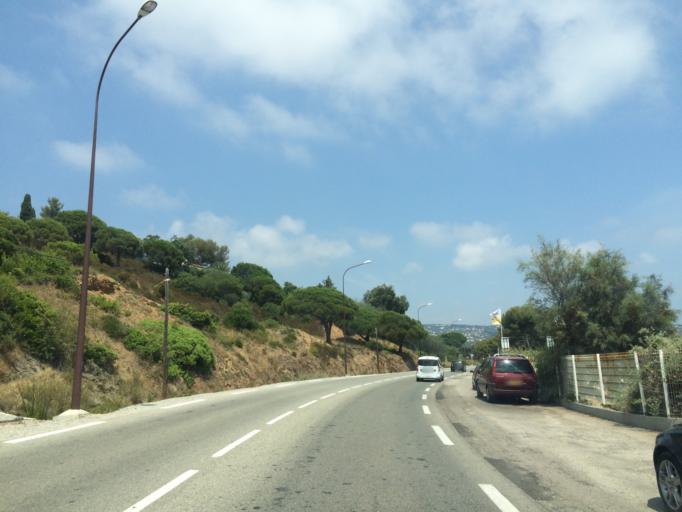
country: FR
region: Provence-Alpes-Cote d'Azur
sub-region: Departement du Var
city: Sainte-Maxime
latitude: 43.3331
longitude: 6.6689
